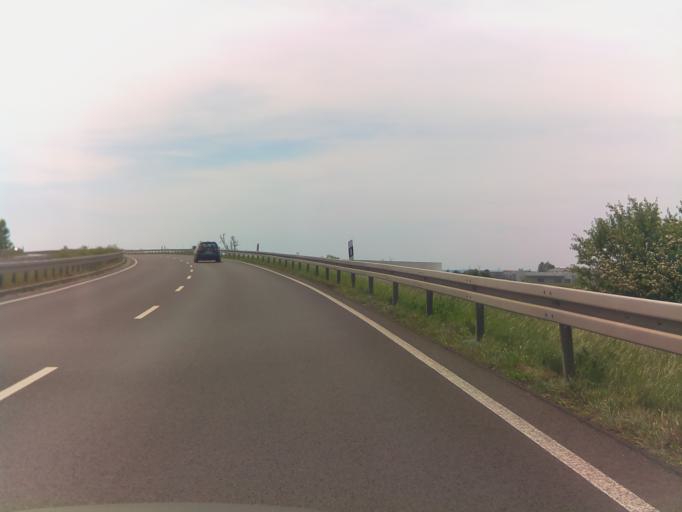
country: DE
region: Saxony-Anhalt
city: Hohendodeleben
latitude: 52.0471
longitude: 11.5203
